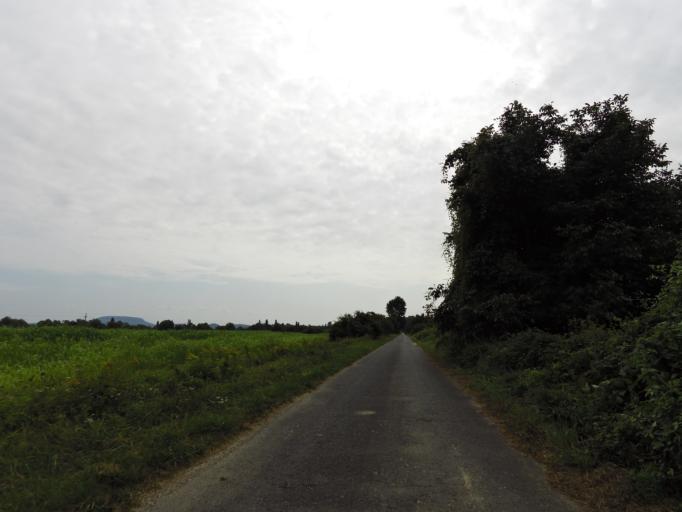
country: HU
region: Veszprem
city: Tapolca
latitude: 46.8441
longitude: 17.3646
